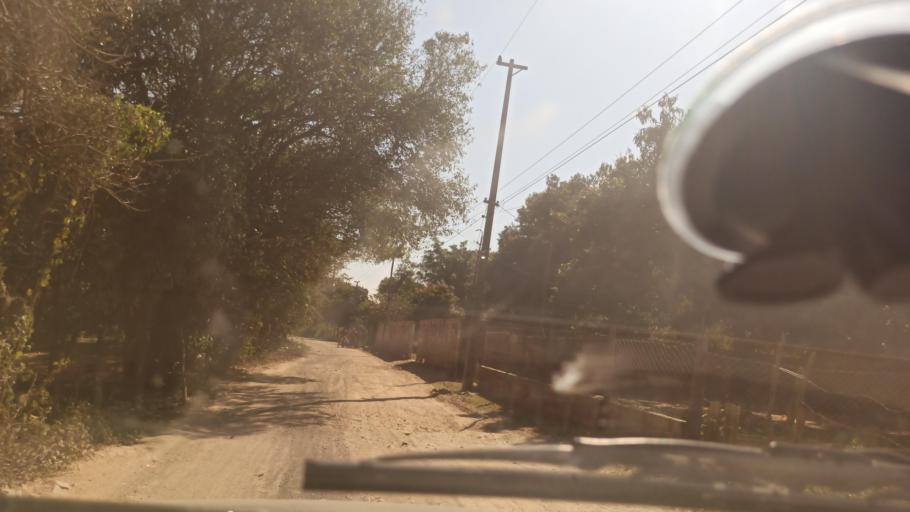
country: AR
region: Formosa
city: Clorinda
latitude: -25.3009
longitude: -57.7040
